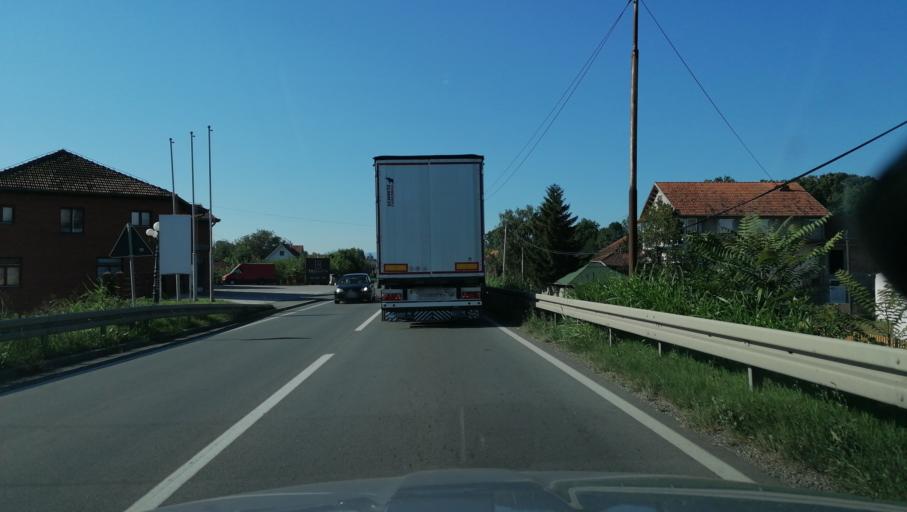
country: RS
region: Central Serbia
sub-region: Raski Okrug
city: Kraljevo
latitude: 43.7480
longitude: 20.6632
